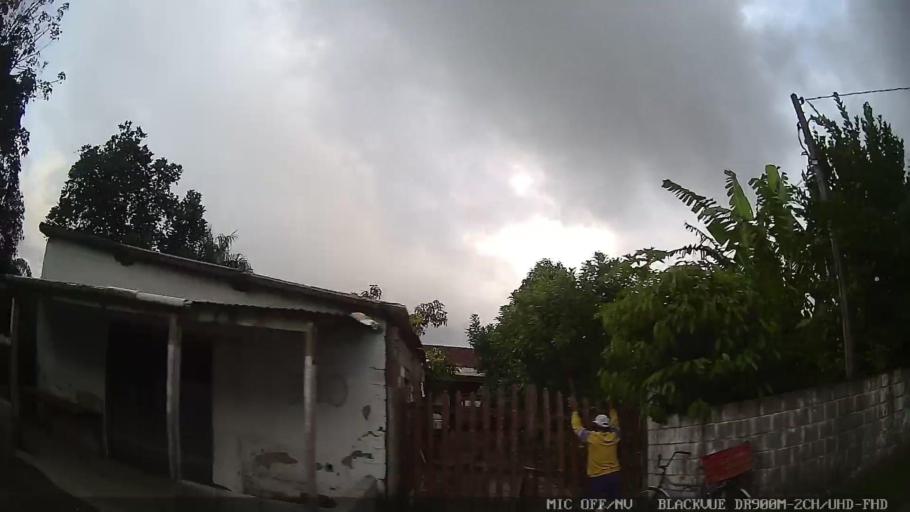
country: BR
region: Sao Paulo
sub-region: Itanhaem
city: Itanhaem
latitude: -24.1023
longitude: -46.8042
